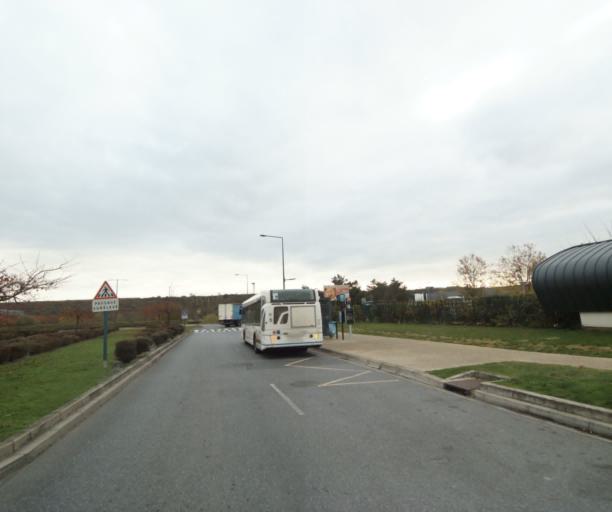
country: FR
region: Ile-de-France
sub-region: Departement de Seine-Saint-Denis
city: Le Blanc-Mesnil
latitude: 48.9622
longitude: 2.4540
